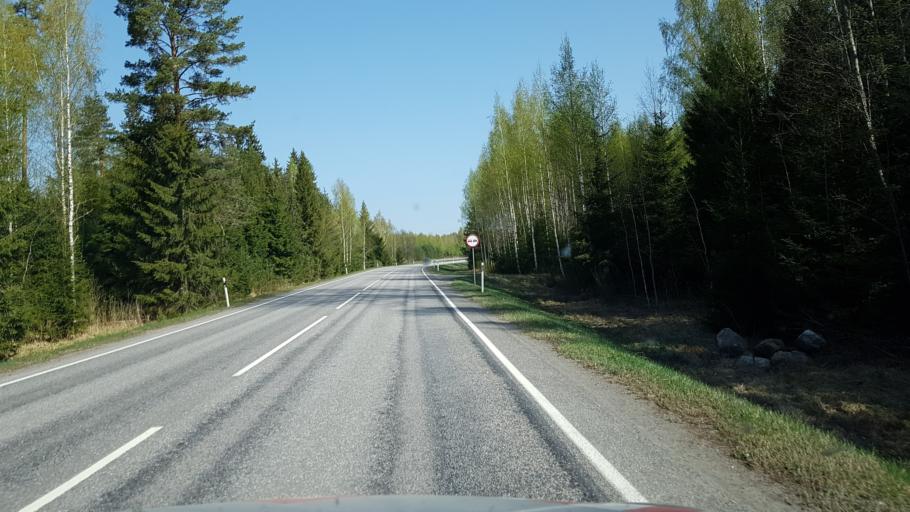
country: EE
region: Paernumaa
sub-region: Saarde vald
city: Kilingi-Nomme
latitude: 58.1886
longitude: 25.0549
